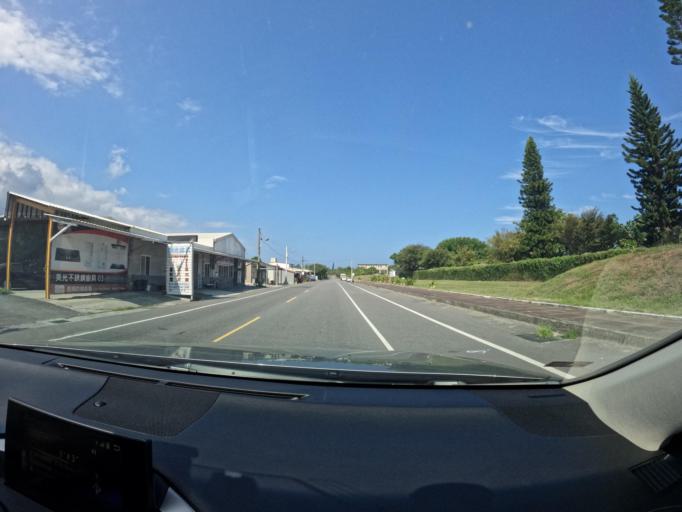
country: TW
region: Taiwan
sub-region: Hualien
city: Hualian
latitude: 24.0122
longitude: 121.6347
